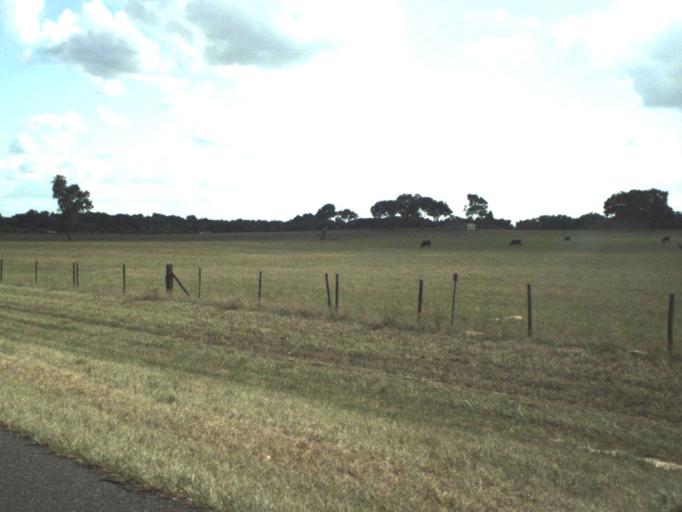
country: US
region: Florida
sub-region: Sumter County
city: The Villages
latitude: 28.9445
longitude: -82.0381
